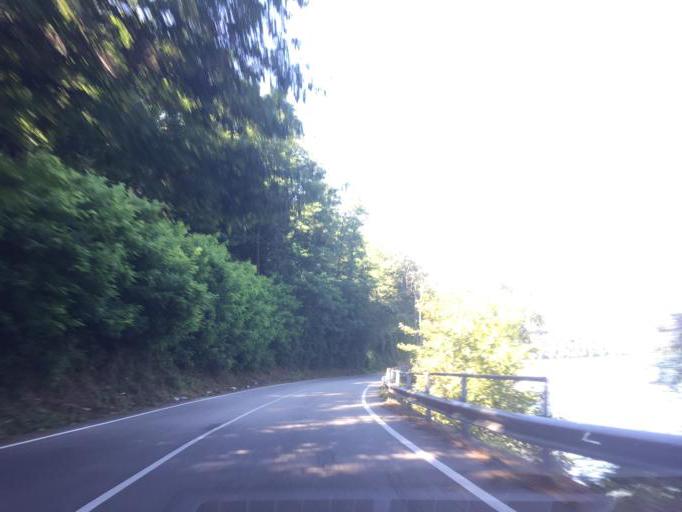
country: IT
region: Lombardy
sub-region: Provincia di Varese
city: Porto Ceresio
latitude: 45.9229
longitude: 8.8912
